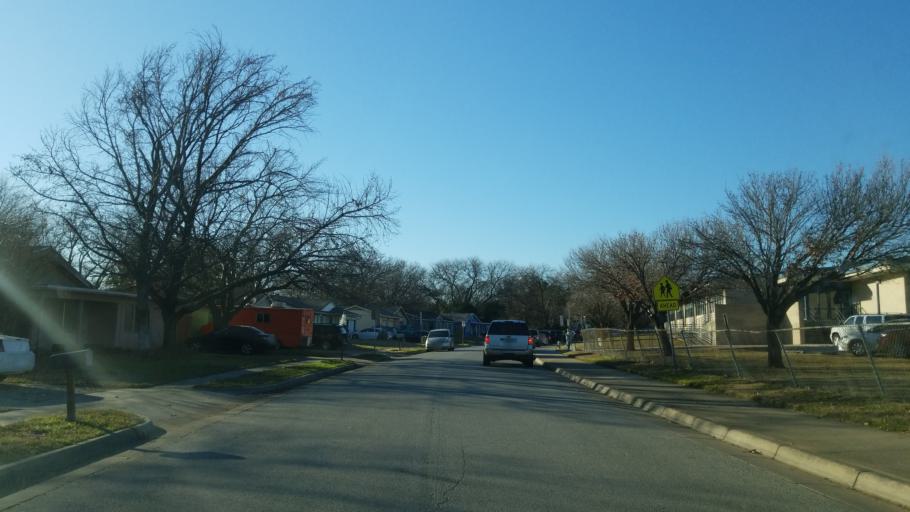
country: US
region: Texas
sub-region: Tarrant County
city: Arlington
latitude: 32.7307
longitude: -97.0651
